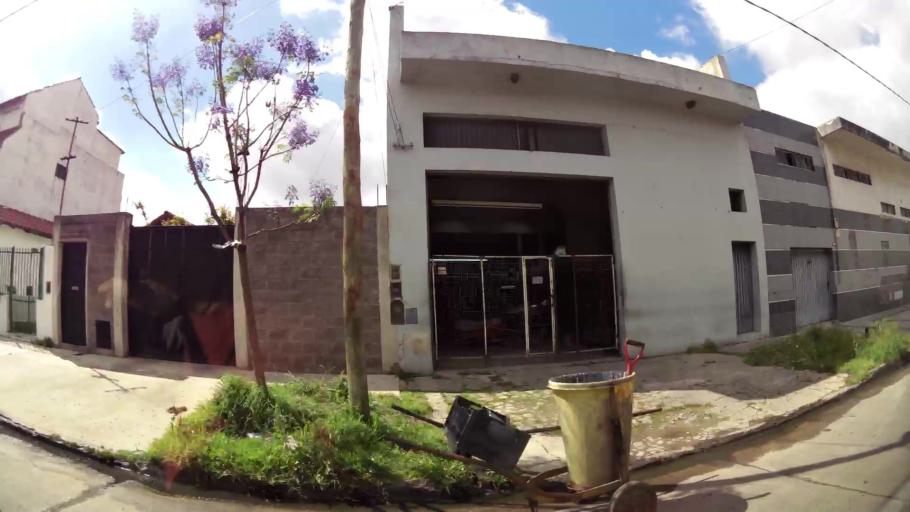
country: AR
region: Buenos Aires
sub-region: Partido de Lanus
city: Lanus
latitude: -34.6877
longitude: -58.4123
